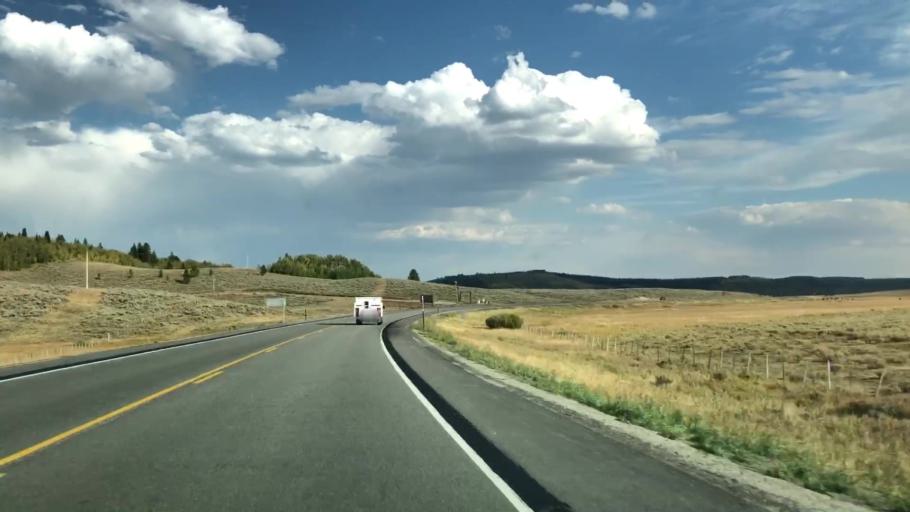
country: US
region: Wyoming
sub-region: Sublette County
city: Pinedale
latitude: 43.1318
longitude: -110.1943
